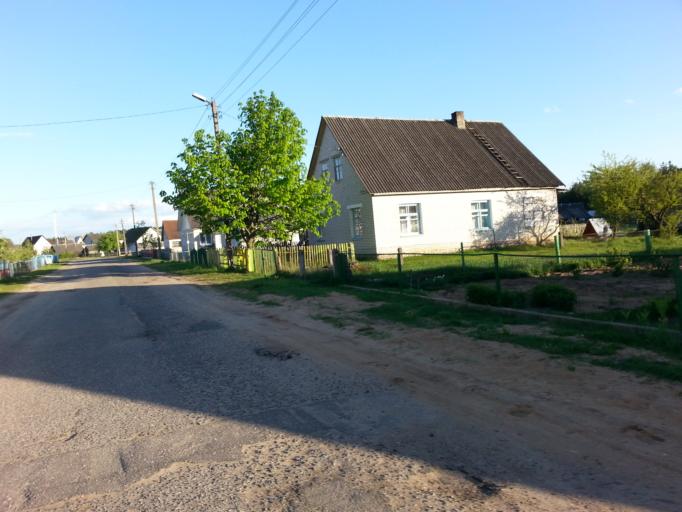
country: BY
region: Minsk
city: Narach
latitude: 54.9294
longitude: 26.6811
